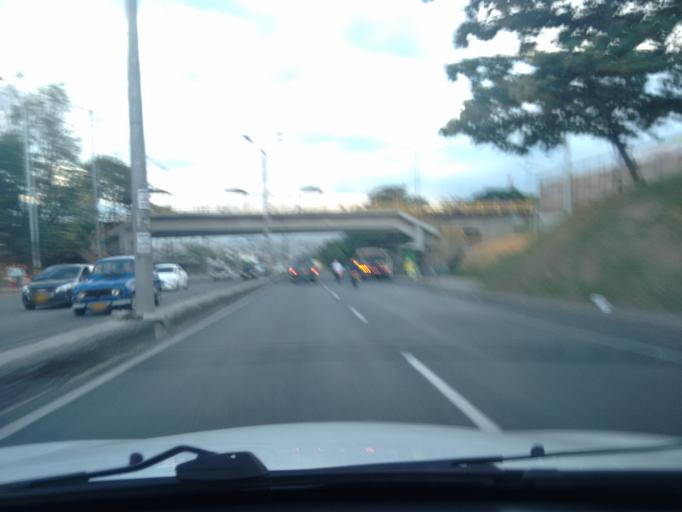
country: CO
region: Antioquia
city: Medellin
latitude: 6.2929
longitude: -75.5682
